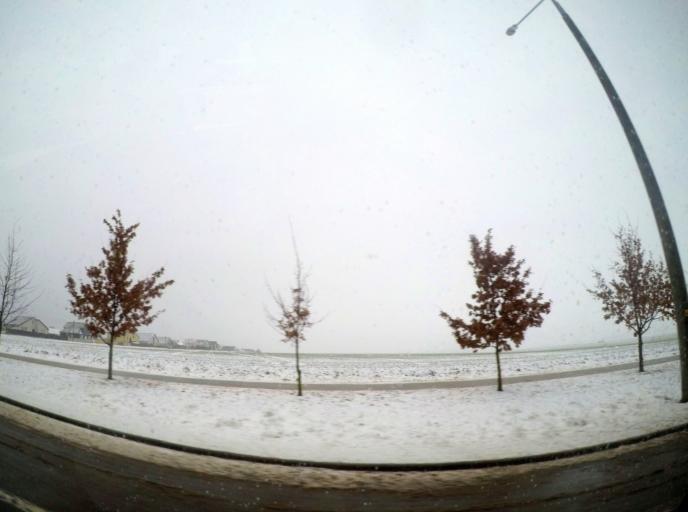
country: BY
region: Grodnenskaya
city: Hrodna
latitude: 53.6243
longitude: 23.8139
